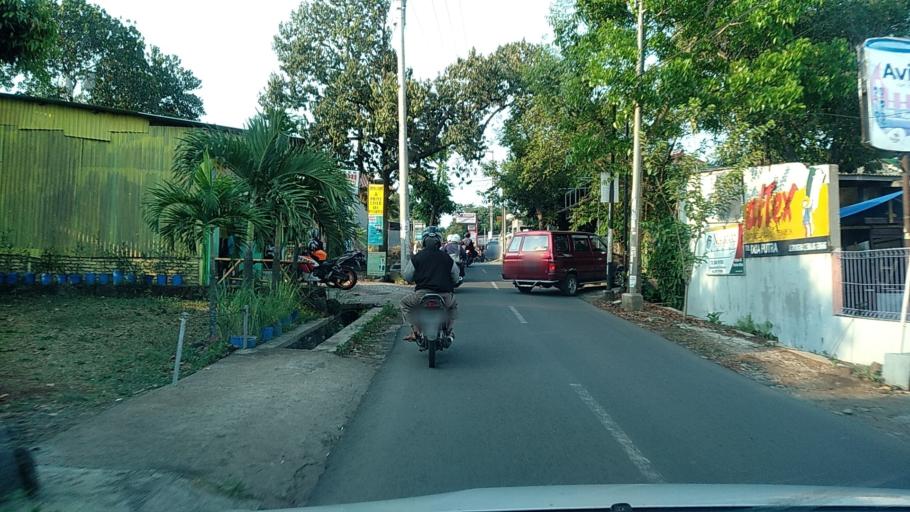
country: ID
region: Central Java
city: Semarang
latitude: -7.0657
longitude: 110.4405
